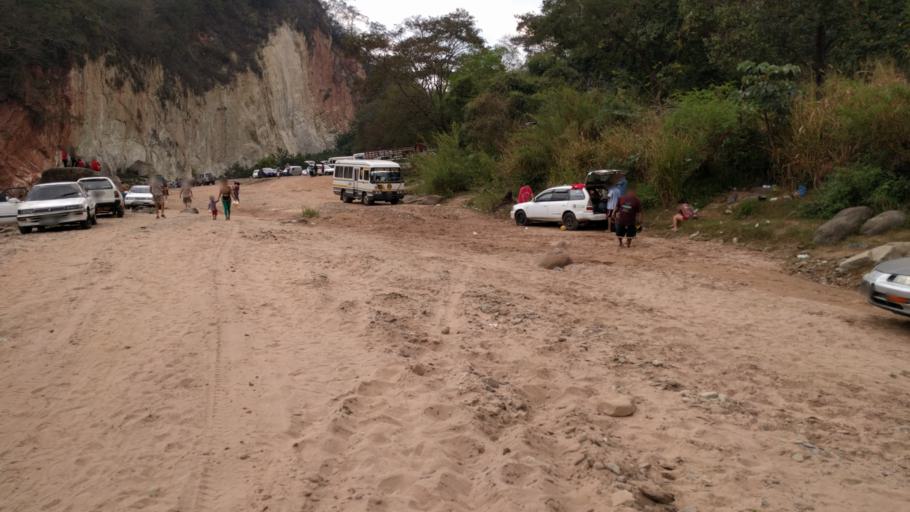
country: BO
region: Santa Cruz
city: Jorochito
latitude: -18.1690
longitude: -63.5270
